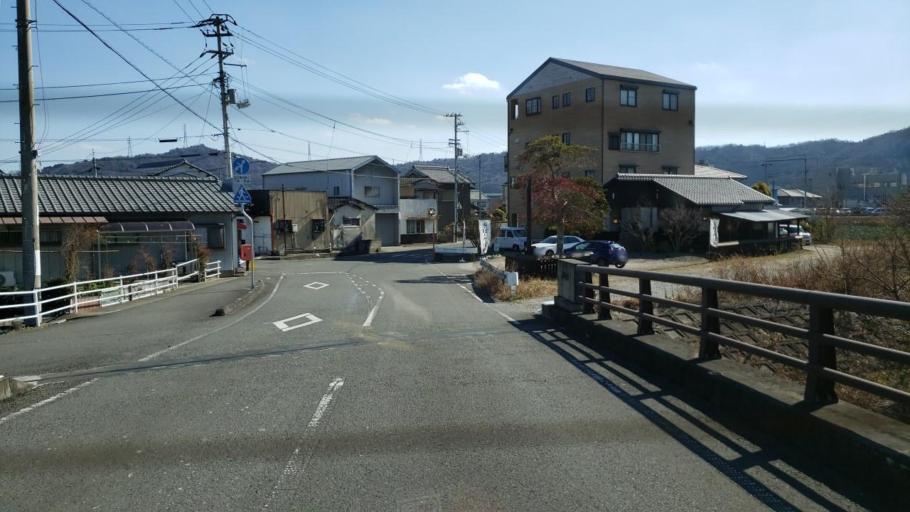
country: JP
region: Tokushima
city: Ishii
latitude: 34.0686
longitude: 134.4366
